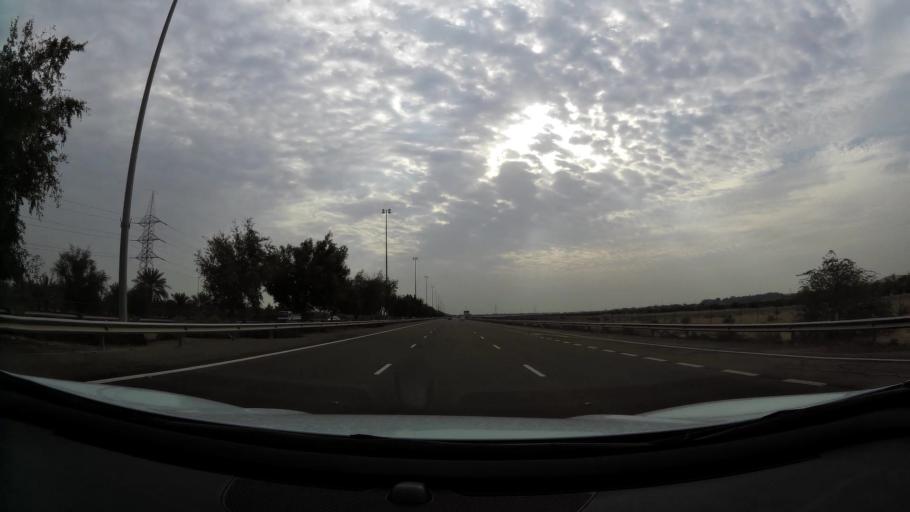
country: AE
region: Abu Dhabi
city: Abu Dhabi
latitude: 24.1891
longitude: 55.0169
